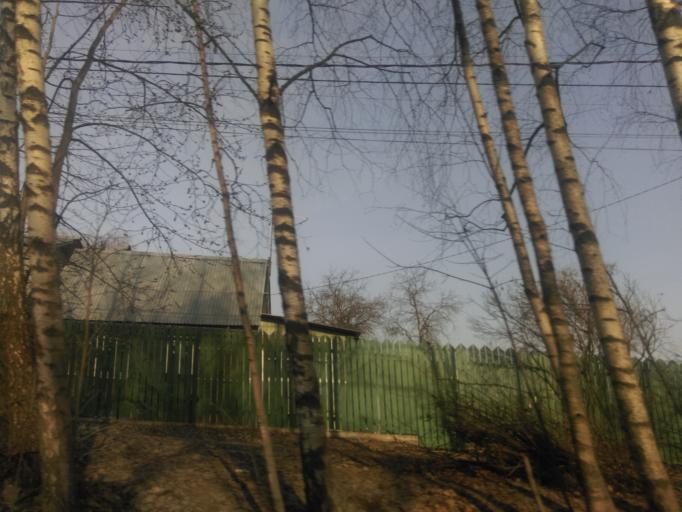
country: RU
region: Moskovskaya
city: Kokoshkino
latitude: 55.5828
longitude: 37.1750
